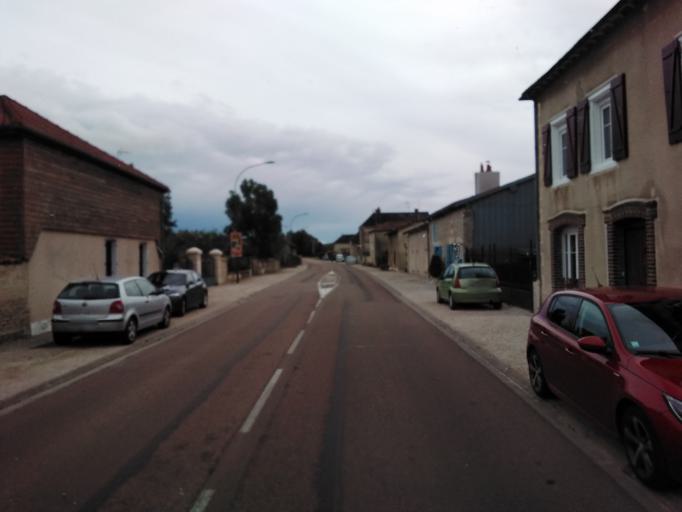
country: FR
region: Champagne-Ardenne
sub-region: Departement de l'Aube
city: Brienne-le-Chateau
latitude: 48.3722
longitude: 4.5301
